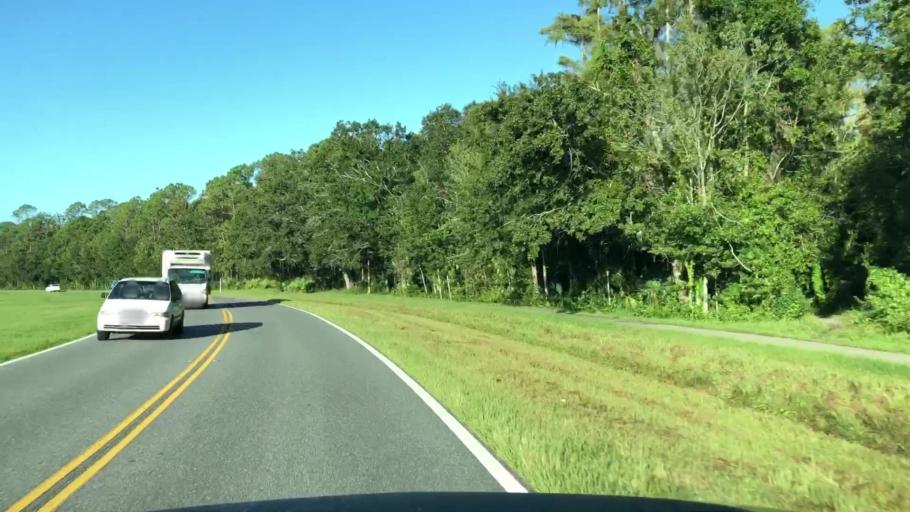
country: US
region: Florida
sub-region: Osceola County
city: Celebration
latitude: 28.3185
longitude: -81.4825
